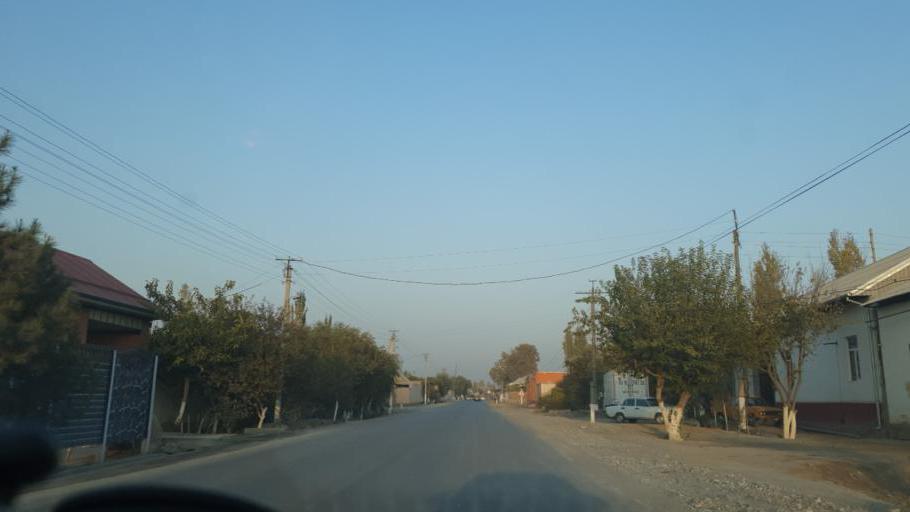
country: UZ
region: Fergana
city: Yaypan
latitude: 40.3757
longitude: 70.7886
